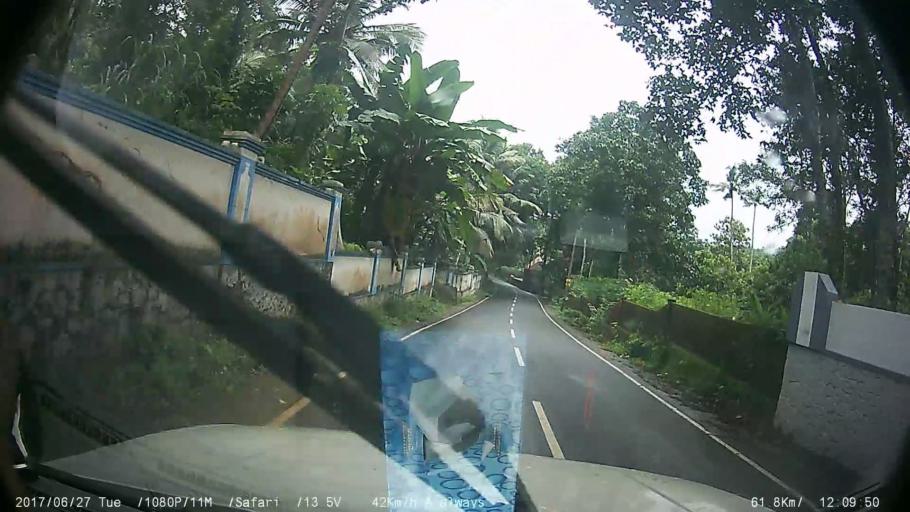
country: IN
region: Kerala
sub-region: Kottayam
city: Palackattumala
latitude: 9.7679
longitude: 76.5521
